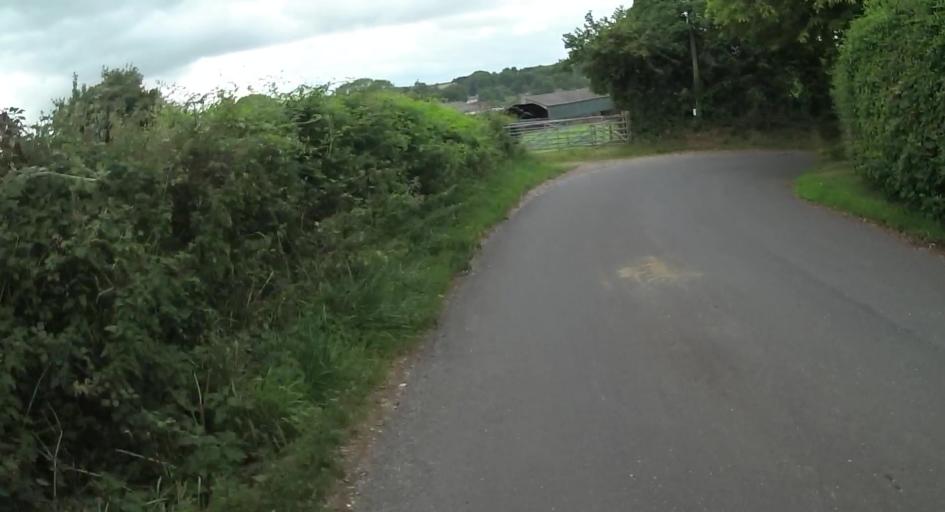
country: GB
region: England
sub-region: Hampshire
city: Four Marks
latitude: 51.0870
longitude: -1.1304
